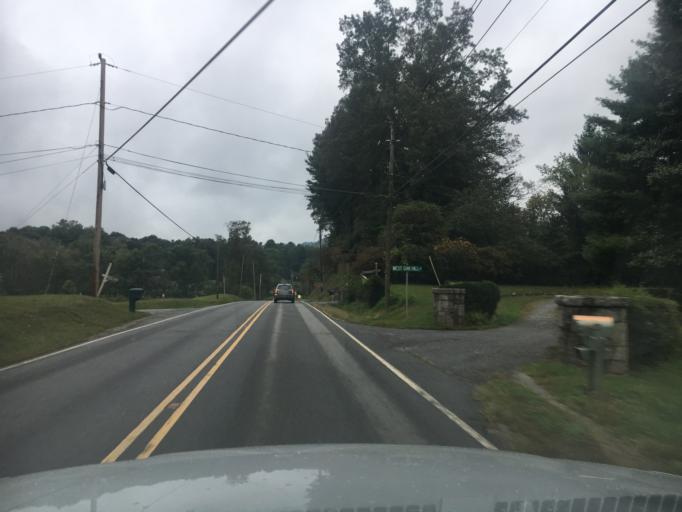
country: US
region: North Carolina
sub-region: Henderson County
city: Horse Shoe
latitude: 35.3369
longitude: -82.5305
